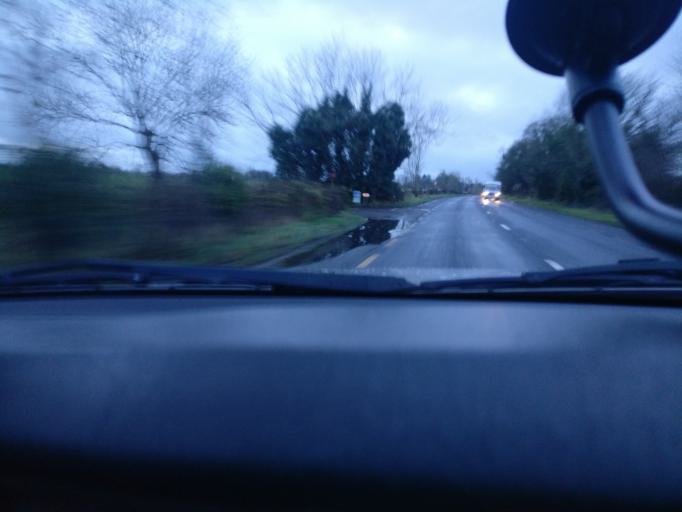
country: IE
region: Connaught
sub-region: County Galway
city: Loughrea
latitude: 53.2478
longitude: -8.4453
